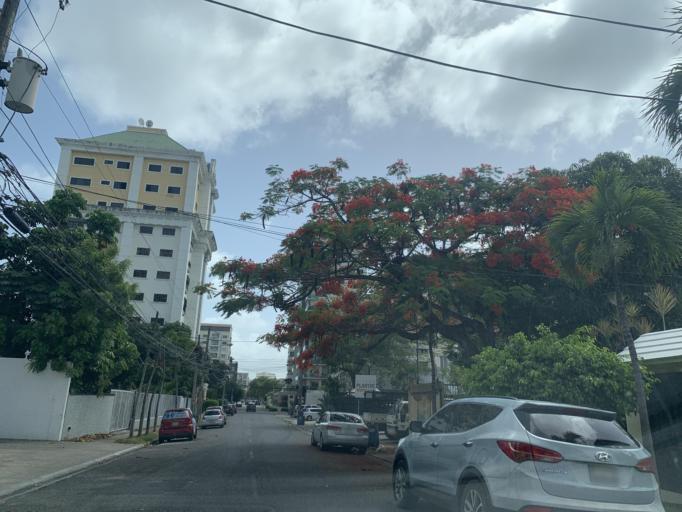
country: DO
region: Nacional
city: La Julia
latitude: 18.4732
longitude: -69.9358
